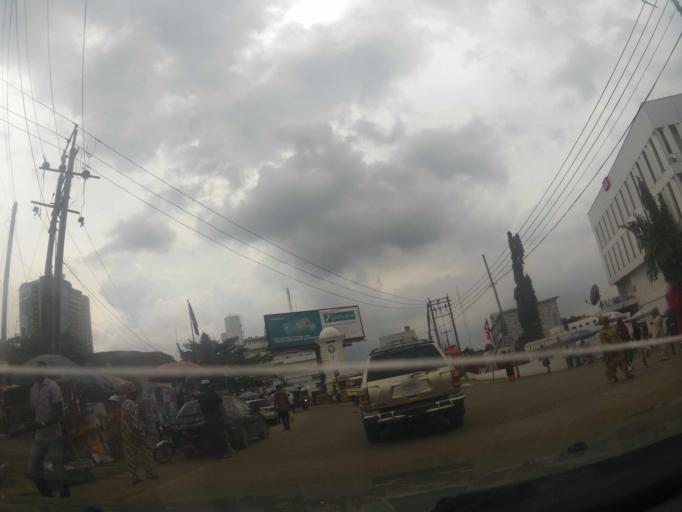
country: NG
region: Oyo
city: Ibadan
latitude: 7.3887
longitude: 3.8811
